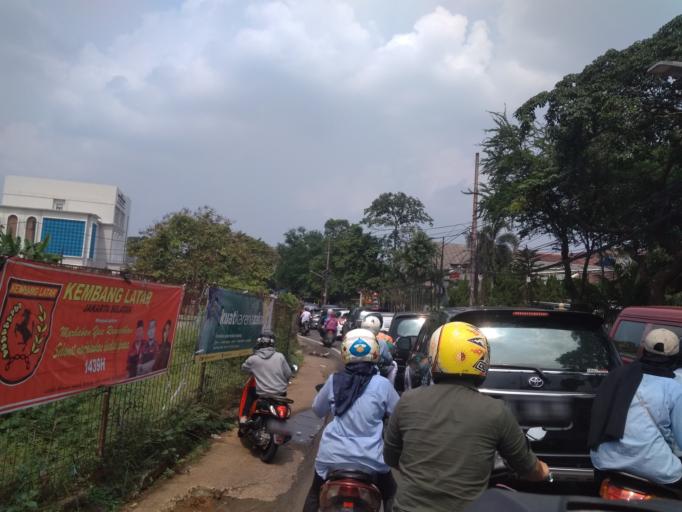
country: ID
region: Banten
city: South Tangerang
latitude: -6.2904
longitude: 106.7709
